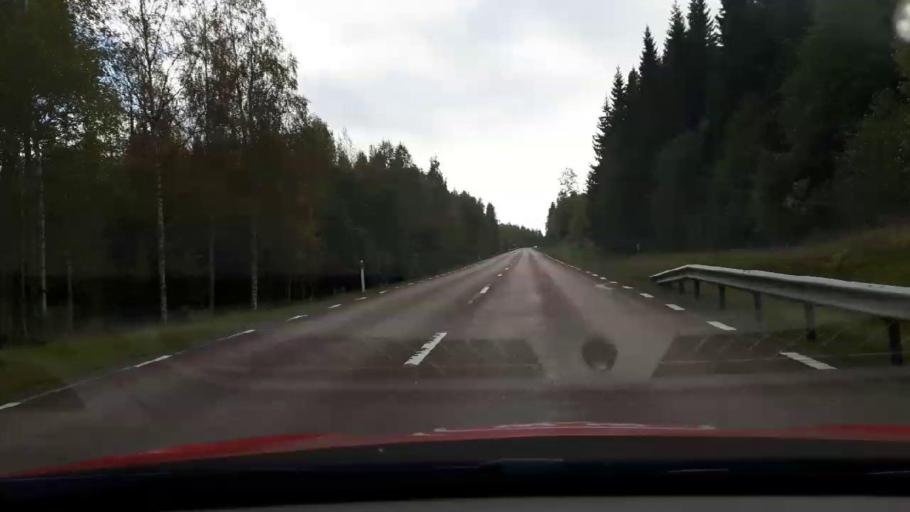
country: SE
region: Gaevleborg
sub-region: Bollnas Kommun
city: Arbra
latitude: 61.5601
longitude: 16.3406
